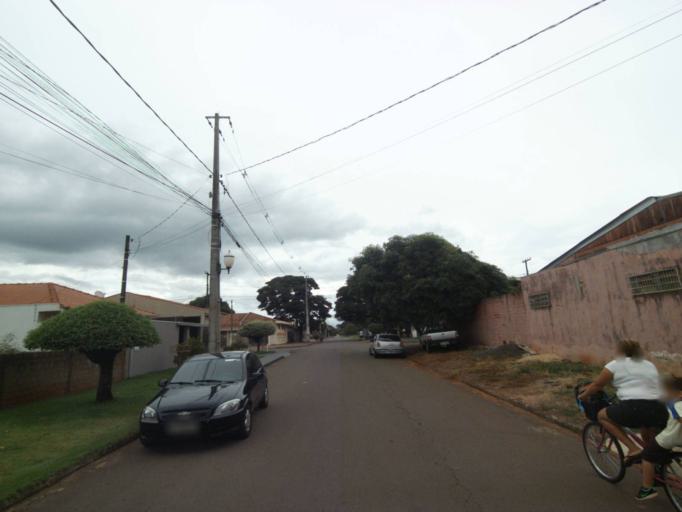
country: BR
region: Parana
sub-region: Campo Mourao
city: Campo Mourao
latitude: -24.0267
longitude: -52.3604
